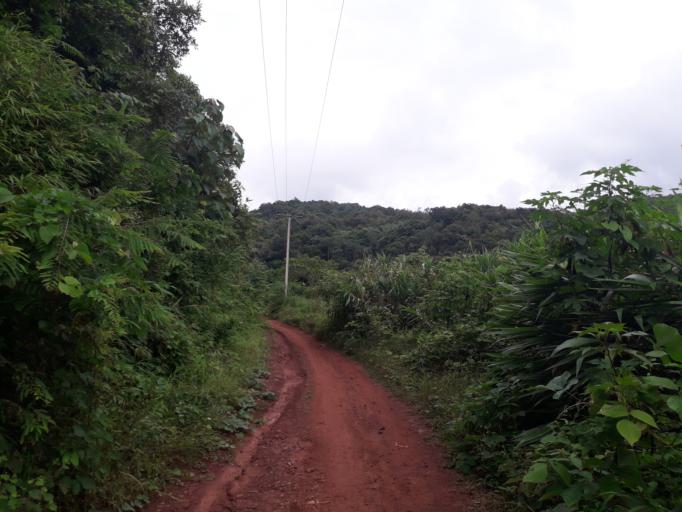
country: CN
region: Yunnan
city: Menglie
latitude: 22.2259
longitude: 101.6285
